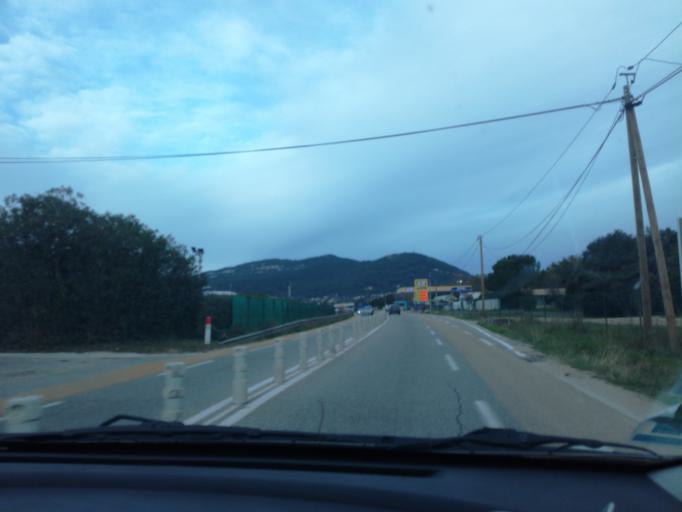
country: FR
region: Provence-Alpes-Cote d'Azur
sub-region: Departement du Var
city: La Crau
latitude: 43.1584
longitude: 6.0653
